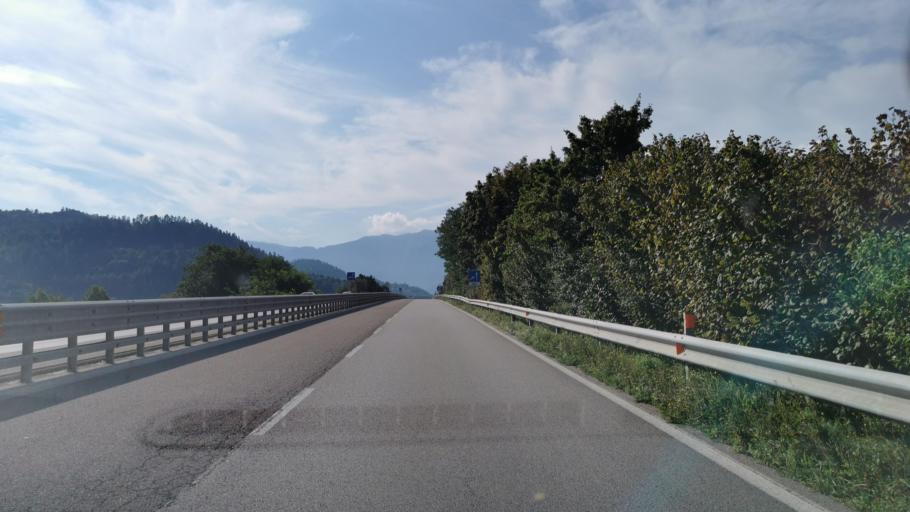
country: IT
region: Trentino-Alto Adige
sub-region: Provincia di Trento
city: Pergine Valsugana
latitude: 46.0534
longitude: 11.2335
